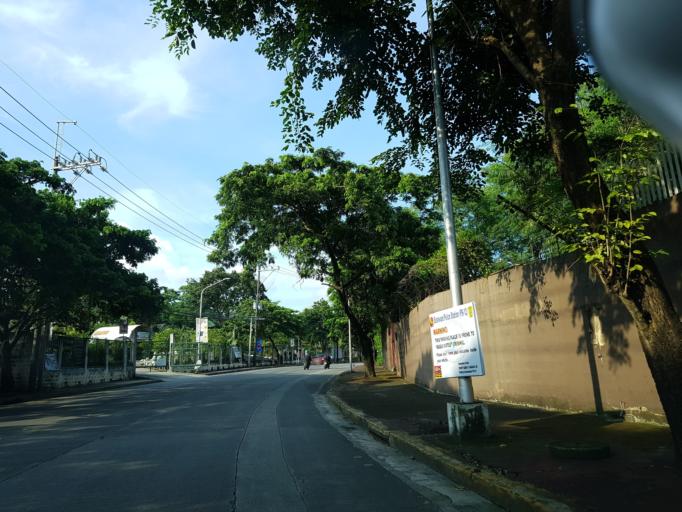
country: PH
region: Metro Manila
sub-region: Pasig
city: Pasig City
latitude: 14.5999
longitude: 121.0711
